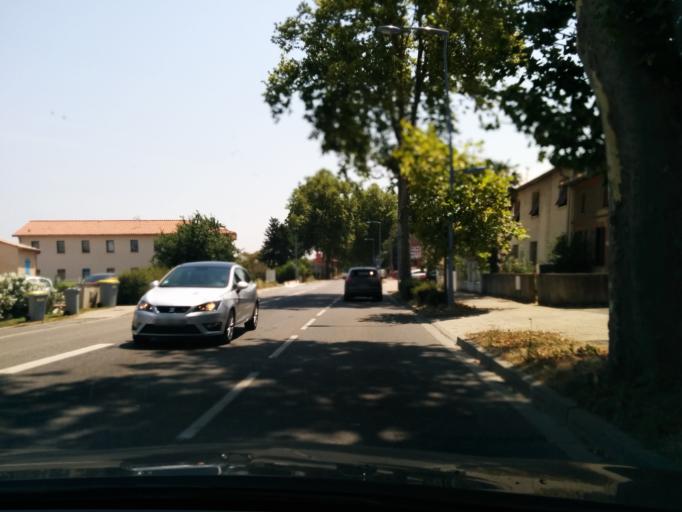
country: FR
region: Midi-Pyrenees
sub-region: Departement de la Haute-Garonne
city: Castanet-Tolosan
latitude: 43.5121
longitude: 1.5013
